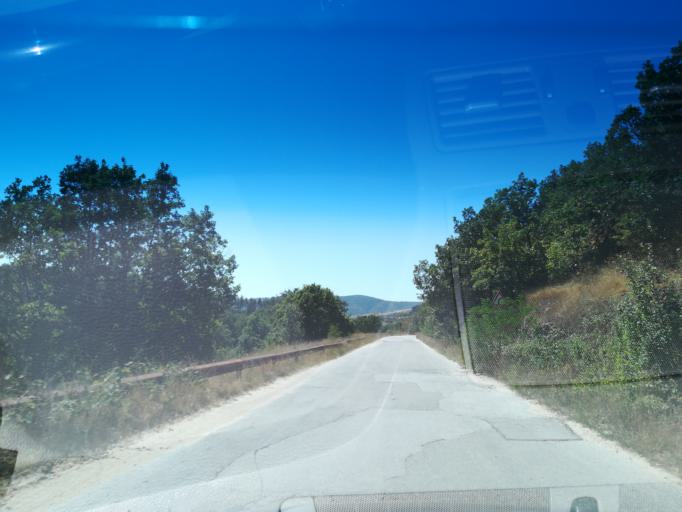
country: BG
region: Pazardzhik
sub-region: Obshtina Strelcha
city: Strelcha
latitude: 42.5258
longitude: 24.3260
